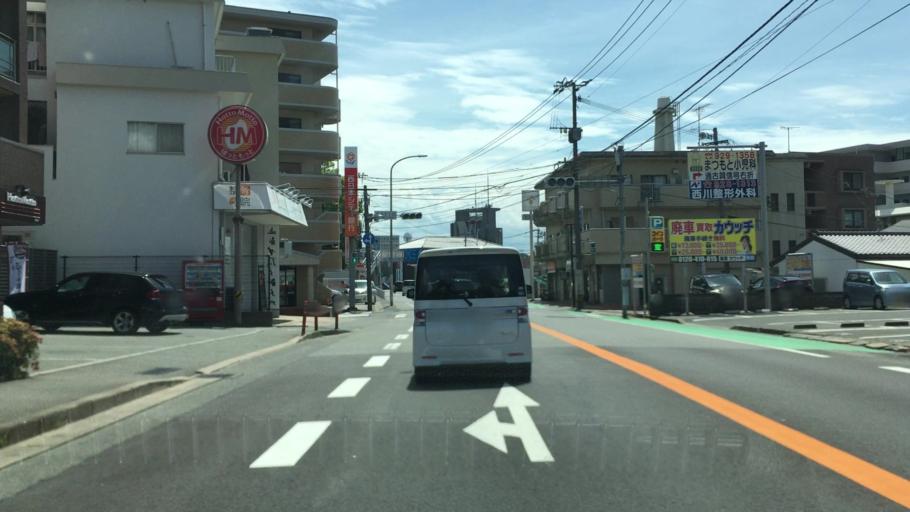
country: JP
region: Fukuoka
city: Dazaifu
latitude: 33.5142
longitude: 130.5068
